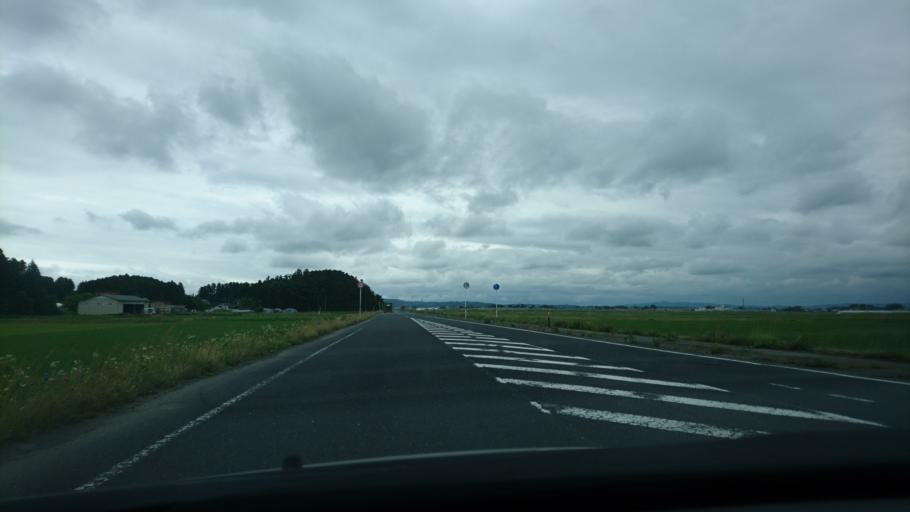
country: JP
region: Miyagi
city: Wakuya
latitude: 38.6988
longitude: 141.2603
